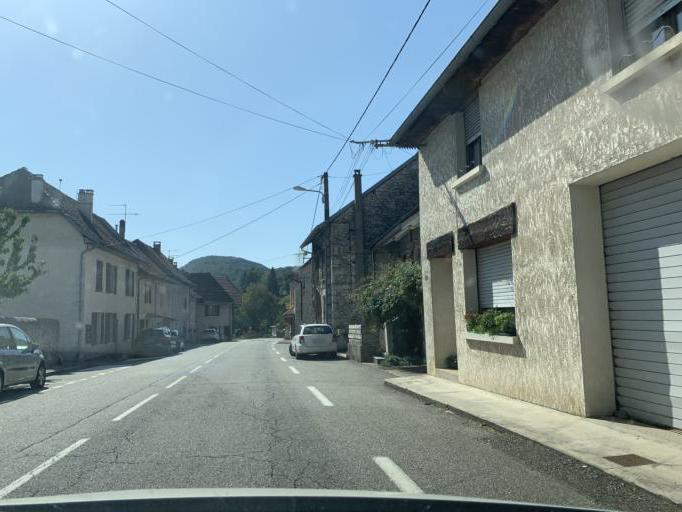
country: FR
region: Rhone-Alpes
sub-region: Departement de la Savoie
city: Yenne
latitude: 45.6791
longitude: 5.6761
